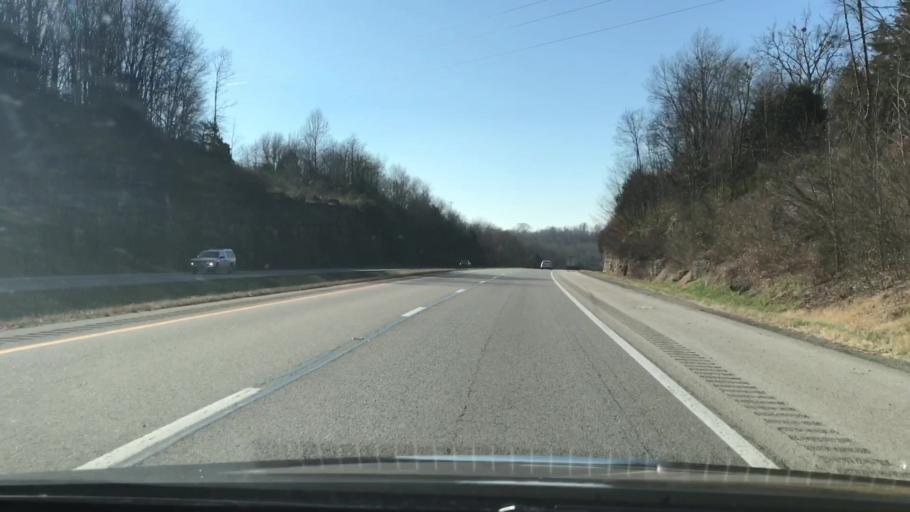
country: US
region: Kentucky
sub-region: Barren County
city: Glasgow
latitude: 36.9783
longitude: -85.9057
